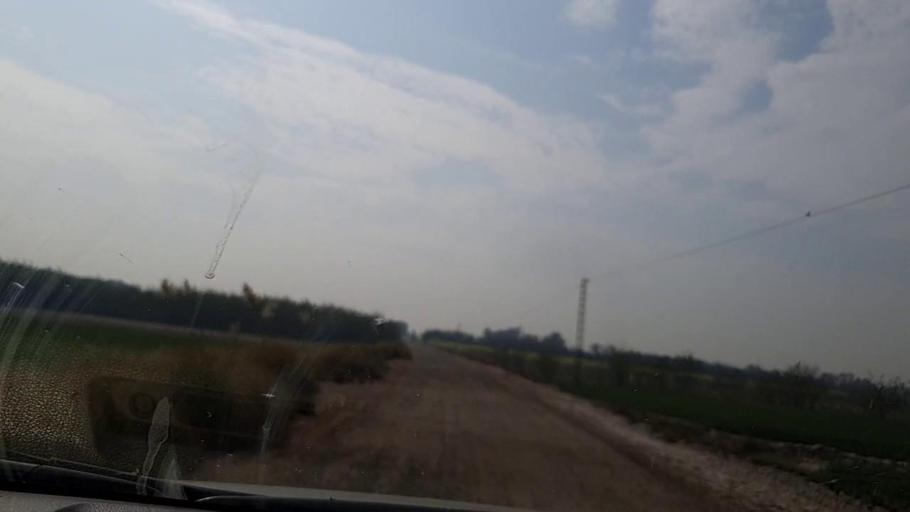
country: PK
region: Sindh
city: Daulatpur
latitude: 26.5293
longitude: 67.9806
